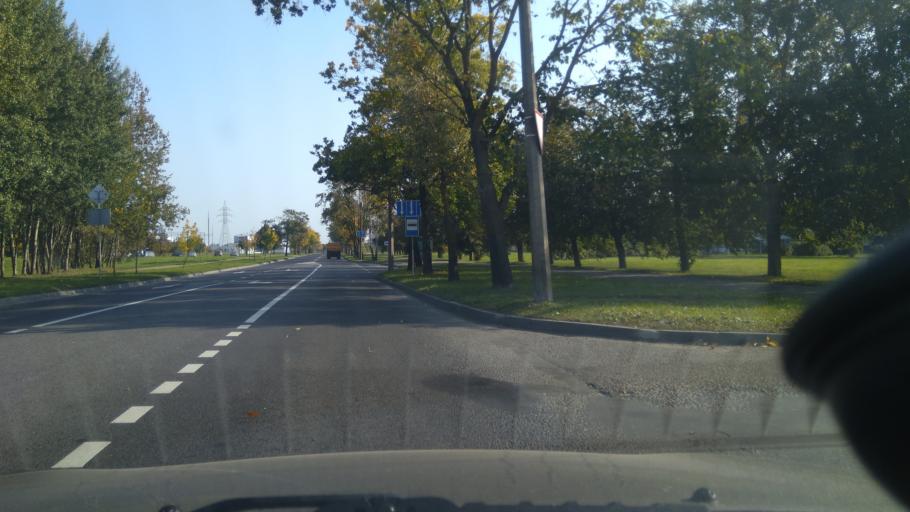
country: BY
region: Minsk
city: Vyaliki Trastsyanets
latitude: 53.8292
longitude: 27.7000
